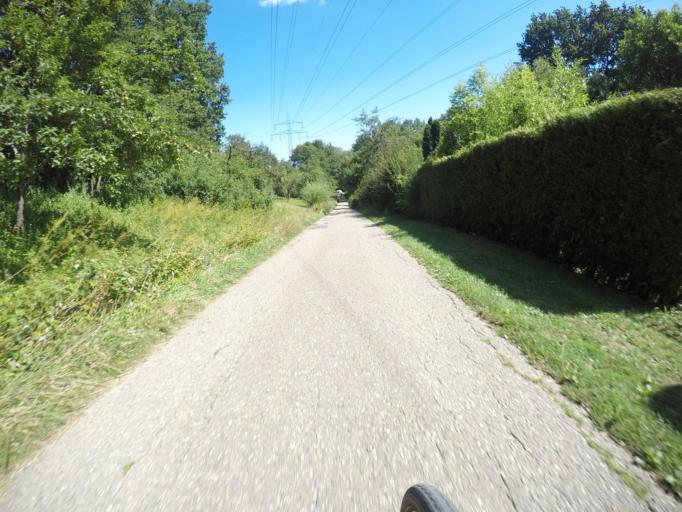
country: DE
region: Baden-Wuerttemberg
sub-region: Regierungsbezirk Stuttgart
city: Leinfelden-Echterdingen
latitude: 48.7047
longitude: 9.1955
